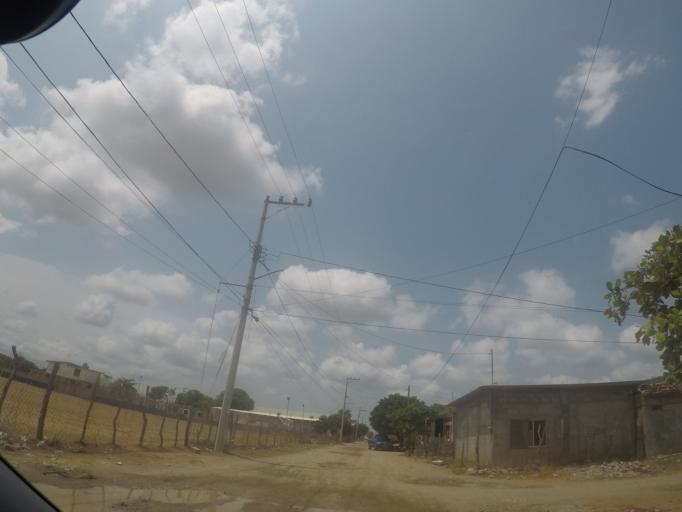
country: MX
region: Oaxaca
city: El Espinal
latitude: 16.5574
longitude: -94.9466
